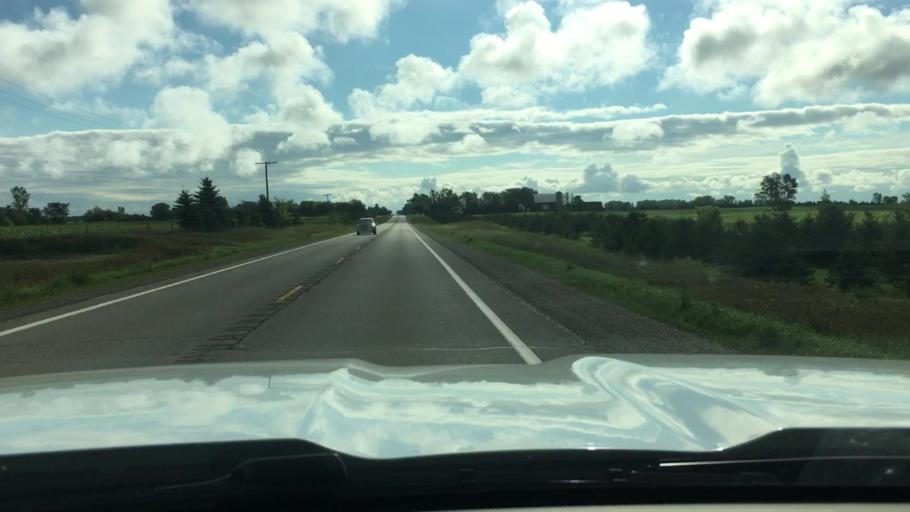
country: US
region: Michigan
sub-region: Tuscola County
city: Cass City
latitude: 43.5993
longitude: -83.2487
